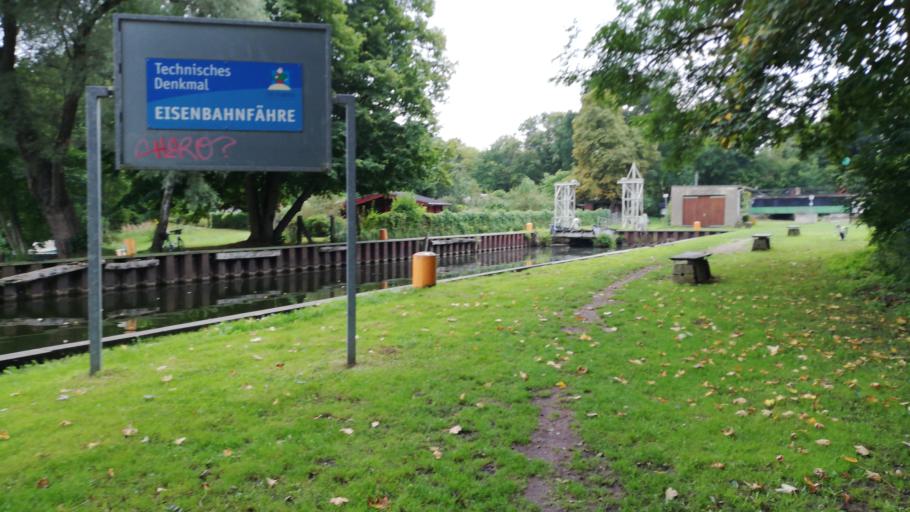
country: DE
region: Brandenburg
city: Furstenberg
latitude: 53.1827
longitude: 13.1602
